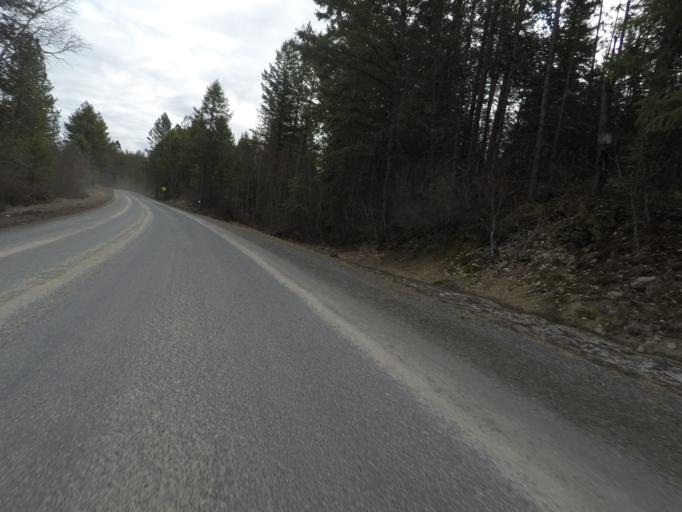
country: US
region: Washington
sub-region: Stevens County
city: Colville
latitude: 48.5032
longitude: -117.8557
